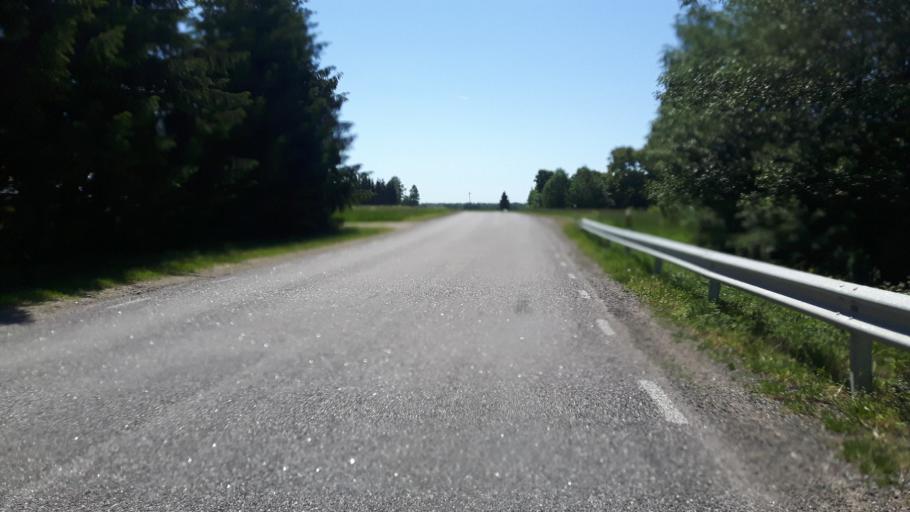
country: EE
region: Paernumaa
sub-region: Tootsi vald
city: Tootsi
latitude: 58.4906
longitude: 24.8378
